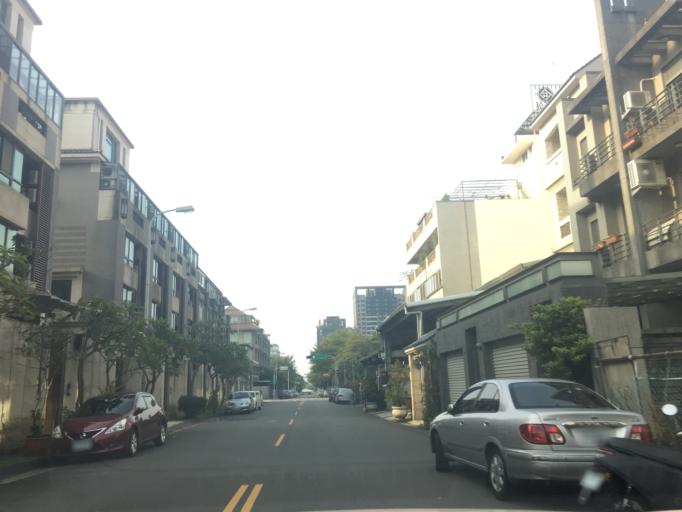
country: TW
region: Taiwan
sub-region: Taichung City
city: Taichung
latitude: 24.1892
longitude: 120.6896
